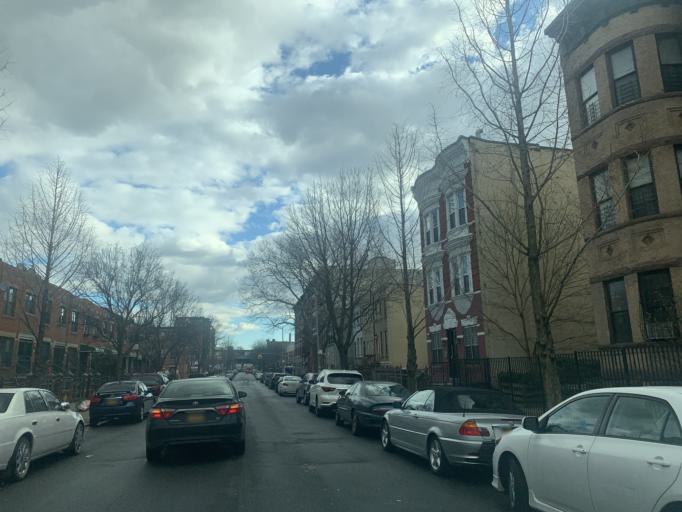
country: US
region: New York
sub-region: Kings County
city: Brooklyn
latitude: 40.6928
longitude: -73.9325
